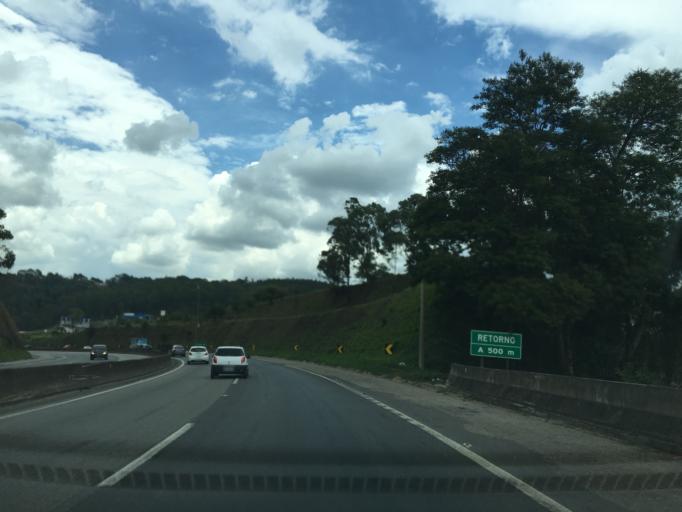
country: BR
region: Sao Paulo
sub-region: Mairipora
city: Mairipora
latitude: -23.2497
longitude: -46.5929
